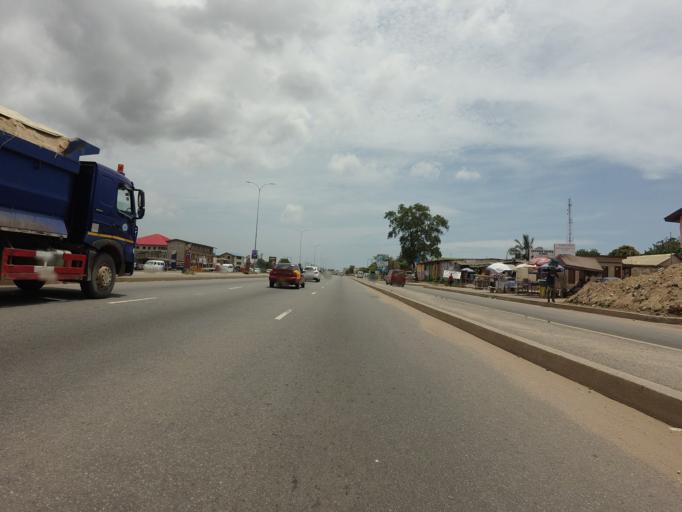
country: GH
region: Greater Accra
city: Accra
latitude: 5.5729
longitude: -0.2488
